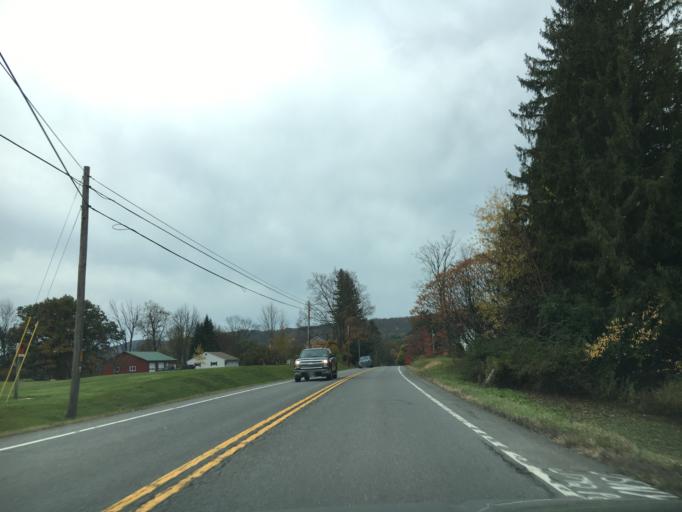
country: US
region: New York
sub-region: Otsego County
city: Cooperstown
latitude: 42.6691
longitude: -74.9554
